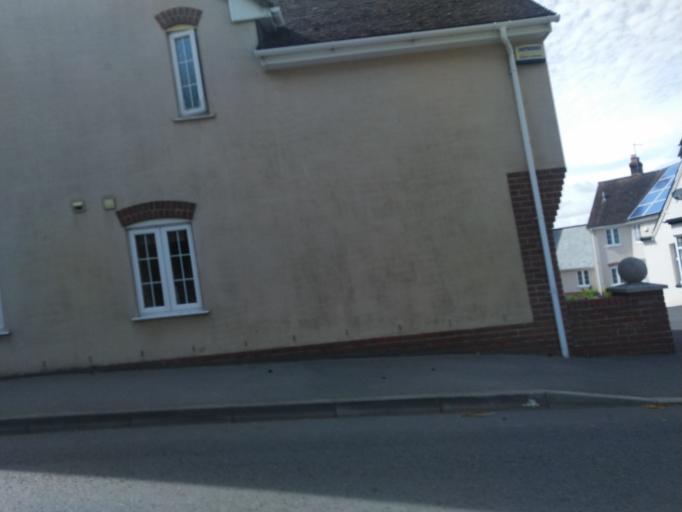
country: GB
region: England
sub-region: Dorset
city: Blandford Forum
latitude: 50.8840
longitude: -2.1980
